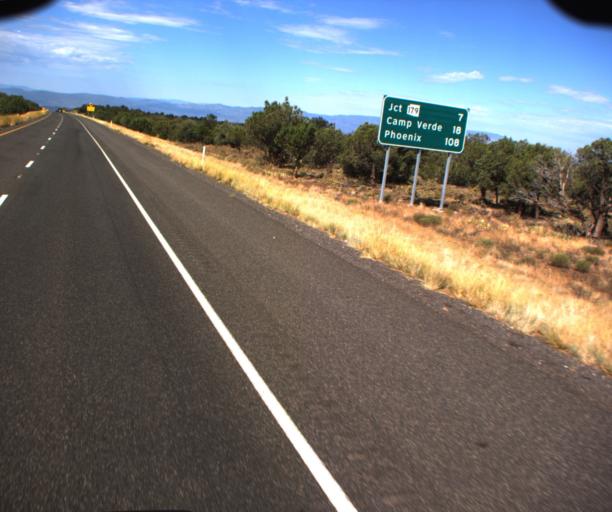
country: US
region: Arizona
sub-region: Yavapai County
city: Village of Oak Creek (Big Park)
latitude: 34.7567
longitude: -111.6678
